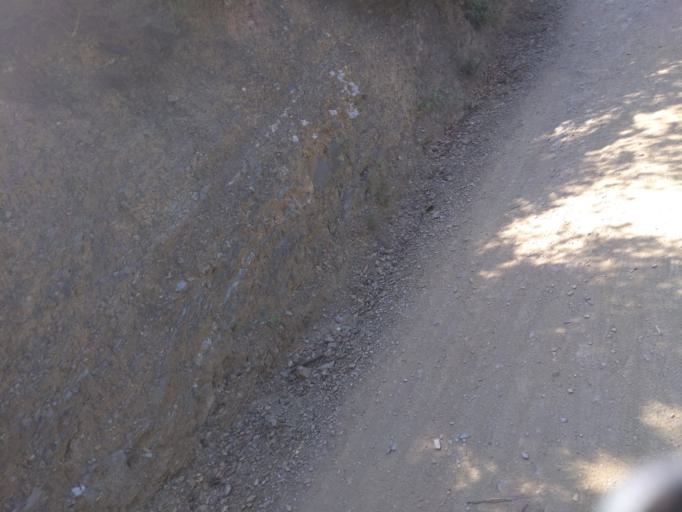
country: ES
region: Catalonia
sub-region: Provincia de Barcelona
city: Nou Barris
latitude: 41.4516
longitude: 2.1548
